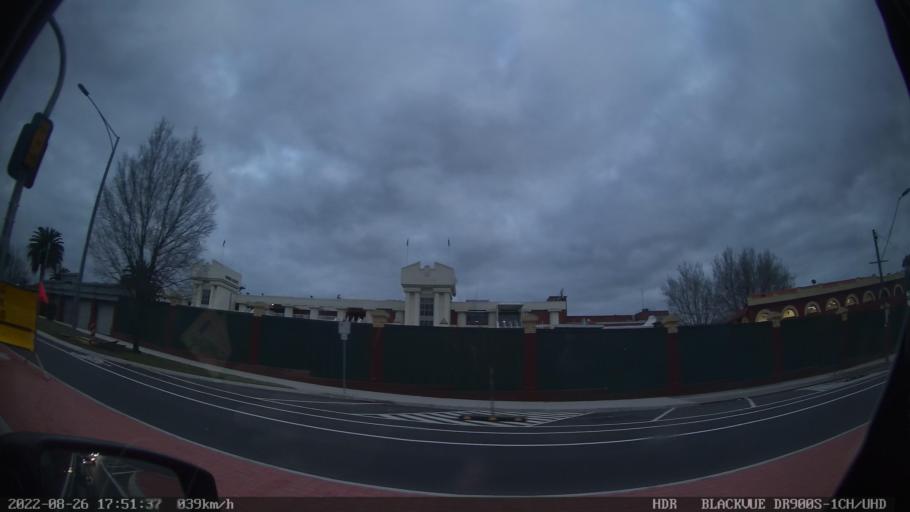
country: AU
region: Victoria
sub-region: Stonnington
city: Malvern East
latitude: -37.8769
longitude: 145.0383
